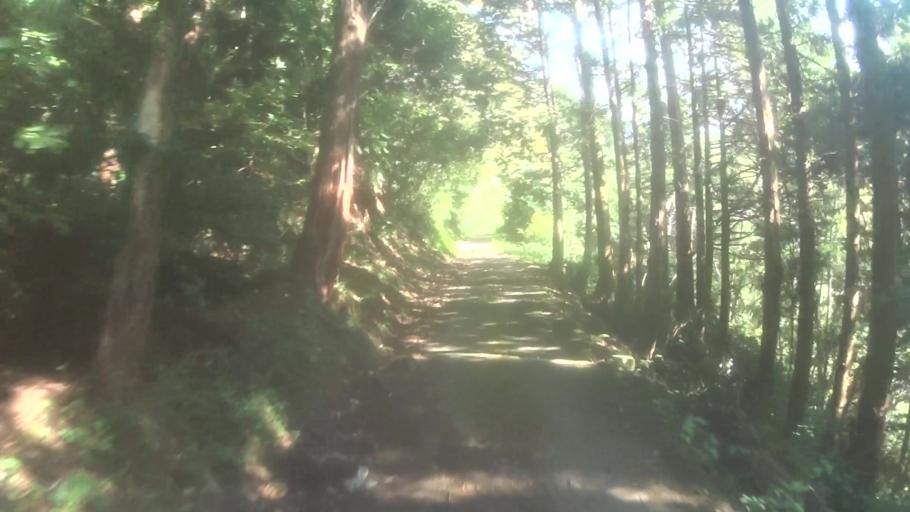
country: JP
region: Kyoto
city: Miyazu
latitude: 35.7159
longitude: 135.1401
